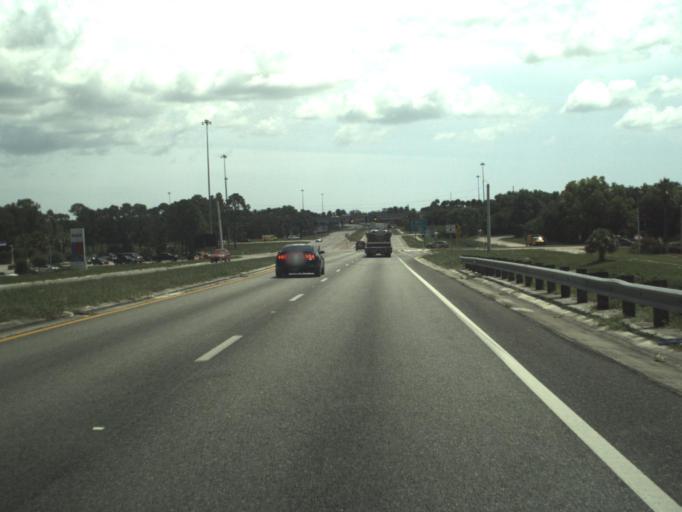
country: US
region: Florida
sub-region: Martin County
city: Palm City
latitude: 27.1054
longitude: -80.2648
